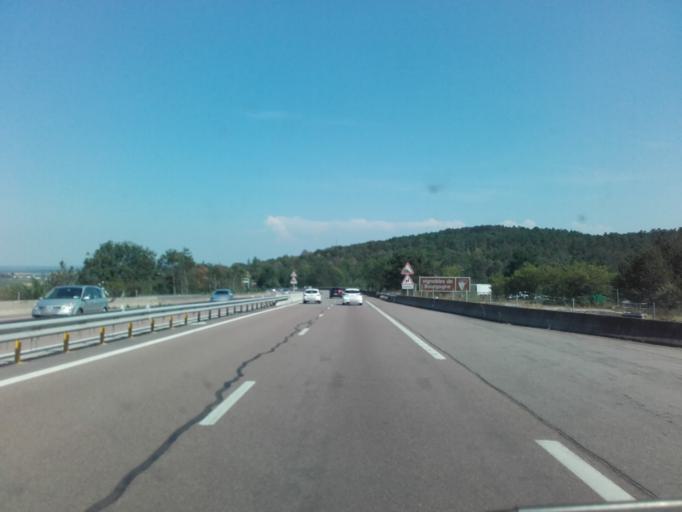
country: FR
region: Bourgogne
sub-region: Departement de la Cote-d'Or
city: Savigny-les-Beaune
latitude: 47.0584
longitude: 4.8127
